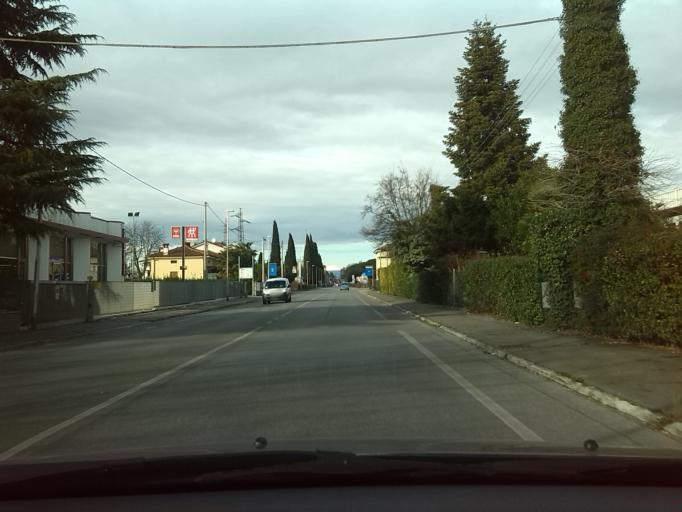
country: IT
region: Friuli Venezia Giulia
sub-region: Provincia di Gorizia
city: Fogliano
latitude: 45.8570
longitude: 13.4845
